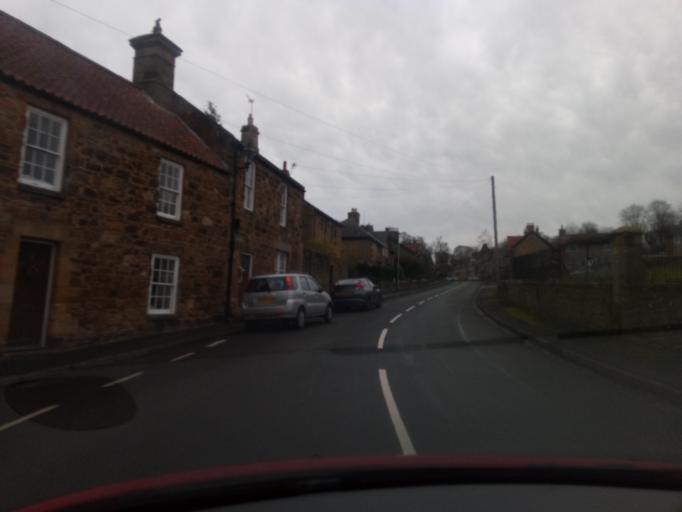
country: GB
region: England
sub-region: Northumberland
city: Alnwick
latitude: 55.4186
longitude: -1.7130
